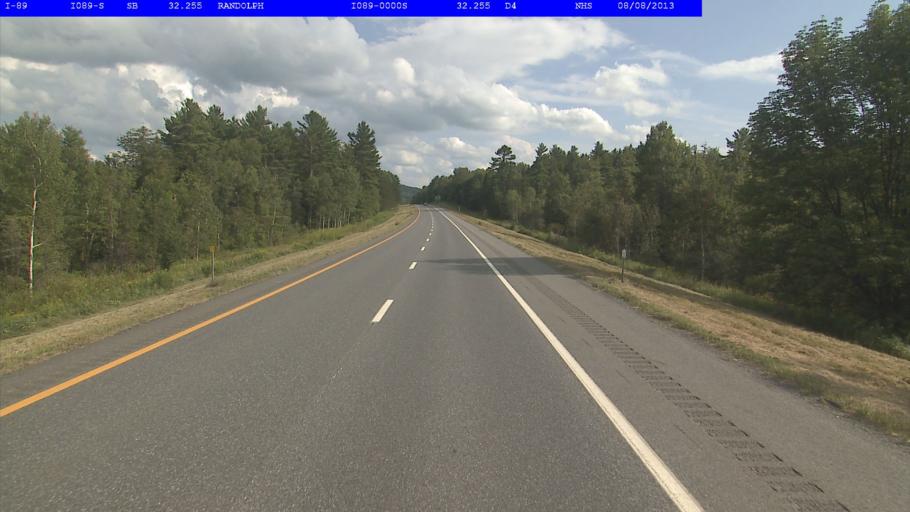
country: US
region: Vermont
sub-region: Orange County
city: Randolph
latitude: 43.9648
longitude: -72.6254
